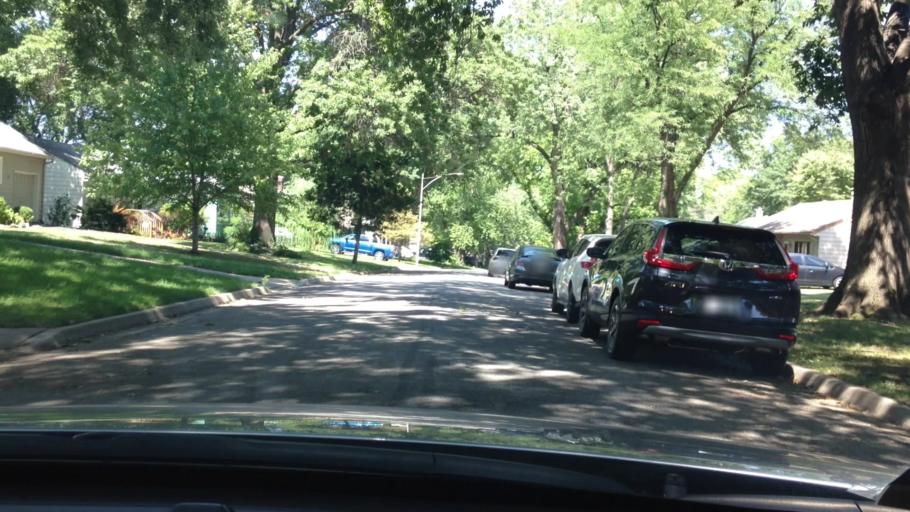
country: US
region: Kansas
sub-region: Johnson County
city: Mission
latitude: 39.0313
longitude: -94.6438
